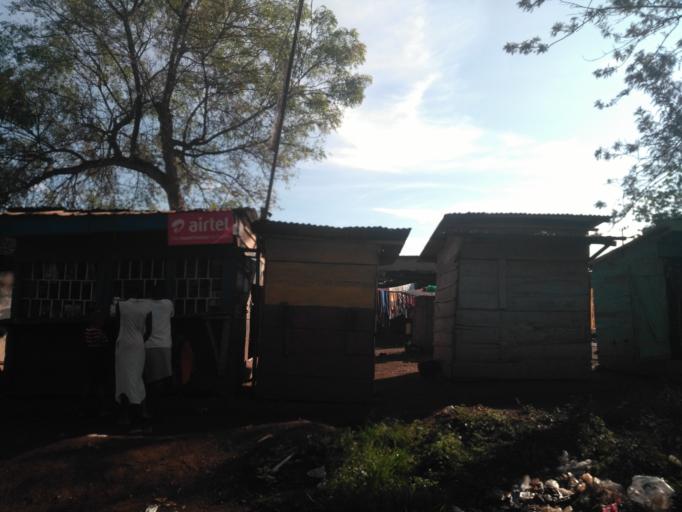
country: UG
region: Eastern Region
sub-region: Jinja District
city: Jinja
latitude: 0.4569
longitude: 33.1854
